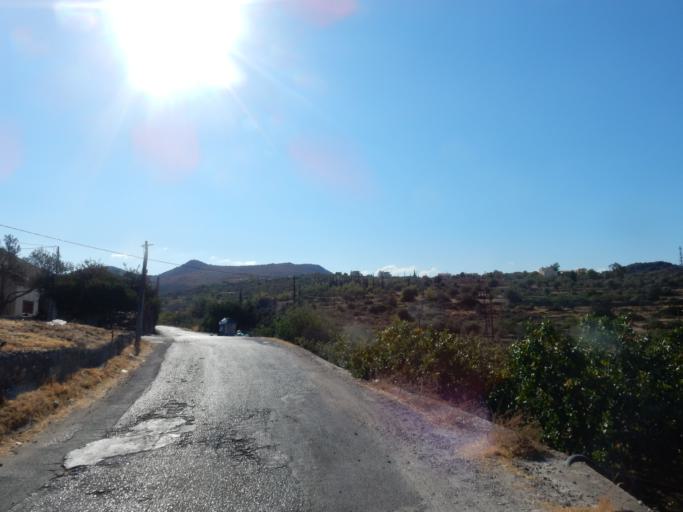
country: GR
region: Attica
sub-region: Nomos Piraios
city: Kypseli
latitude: 37.7349
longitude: 23.4530
